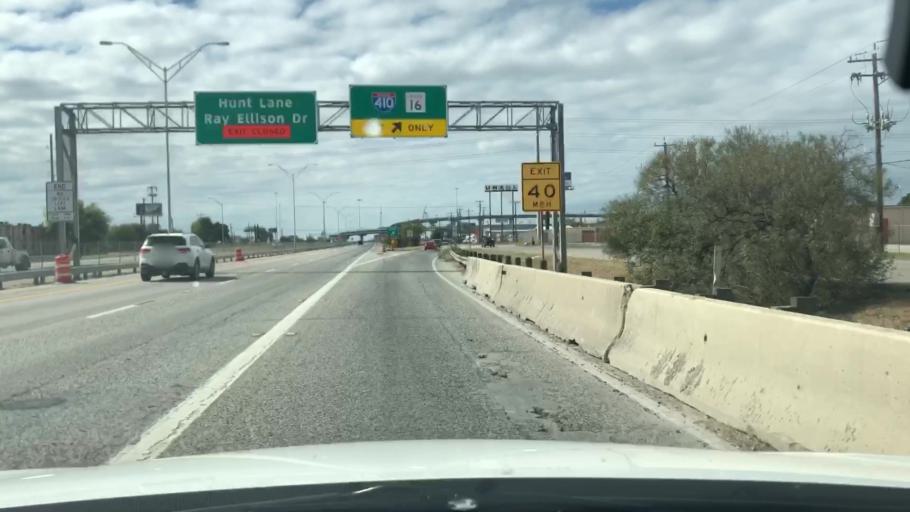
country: US
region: Texas
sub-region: Bexar County
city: Lackland Air Force Base
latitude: 29.3995
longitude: -98.6415
